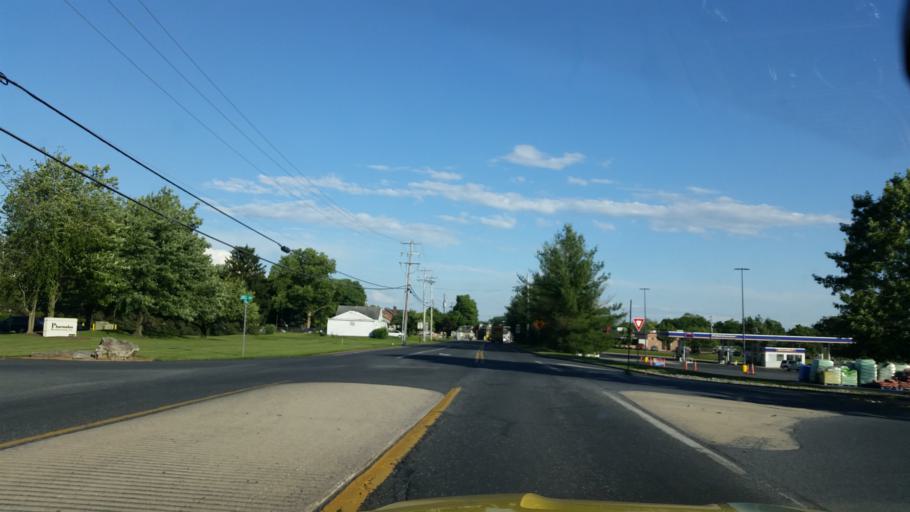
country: US
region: Pennsylvania
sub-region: Lebanon County
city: Avon
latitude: 40.3507
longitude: -76.3885
